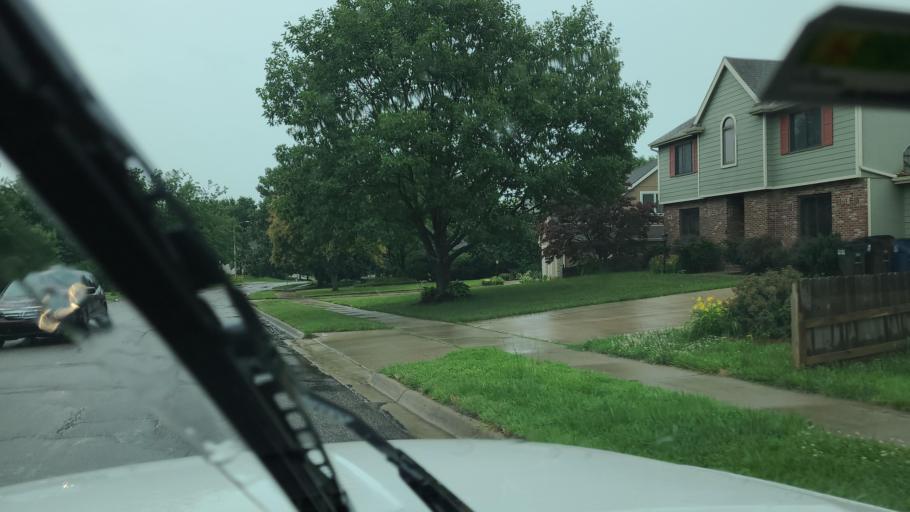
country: US
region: Kansas
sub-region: Douglas County
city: Lawrence
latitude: 38.9652
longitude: -95.2947
